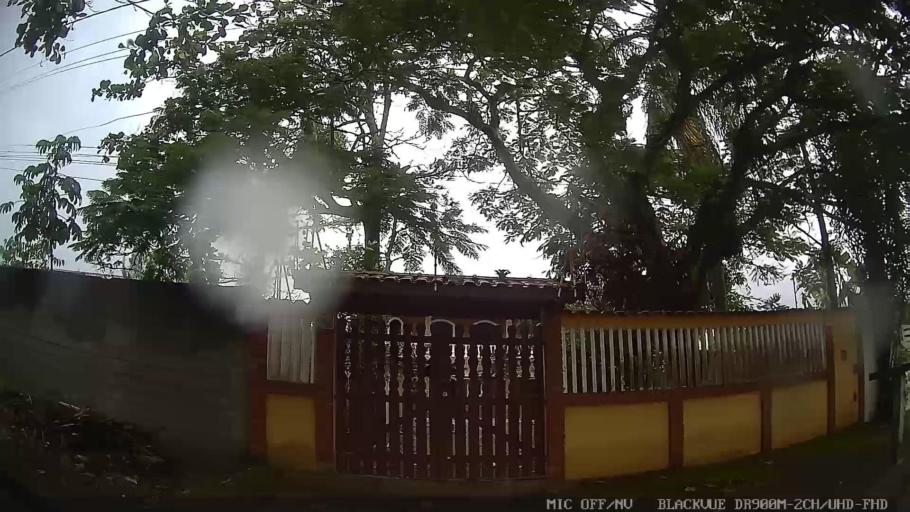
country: BR
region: Sao Paulo
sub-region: Itanhaem
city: Itanhaem
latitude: -24.2161
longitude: -46.8577
